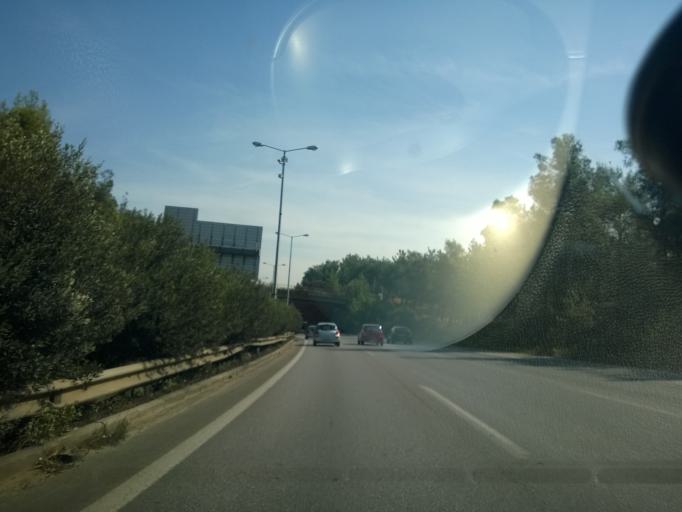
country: GR
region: Central Macedonia
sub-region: Nomos Thessalonikis
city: Triandria
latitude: 40.6146
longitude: 22.9872
